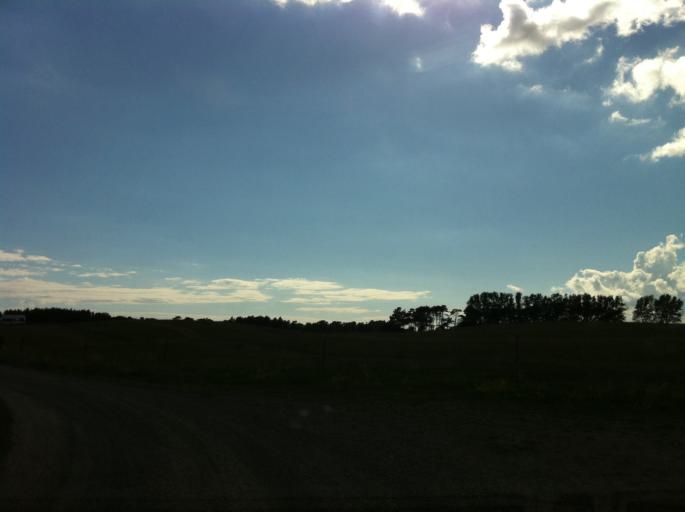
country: SE
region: Skane
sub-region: Ystads Kommun
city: Kopingebro
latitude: 55.3909
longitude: 14.0511
